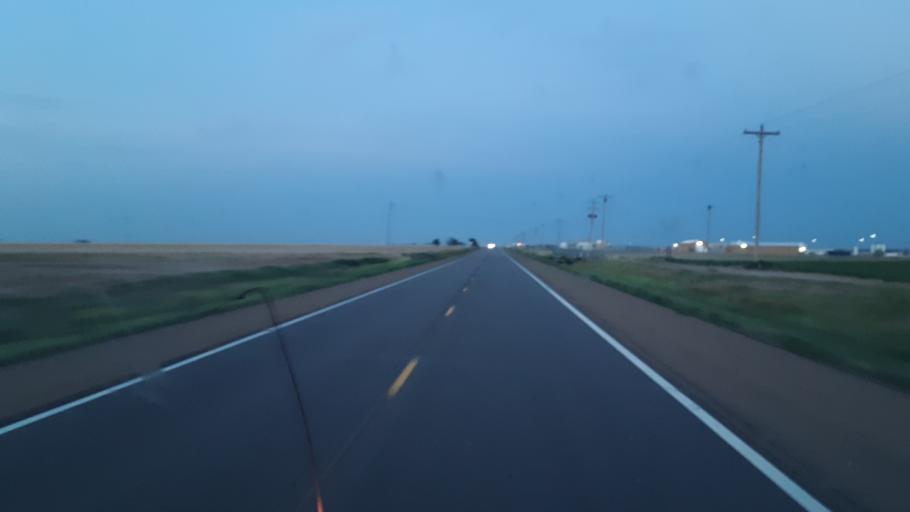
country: US
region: Kansas
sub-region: Finney County
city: Holcomb
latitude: 38.0034
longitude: -101.0410
